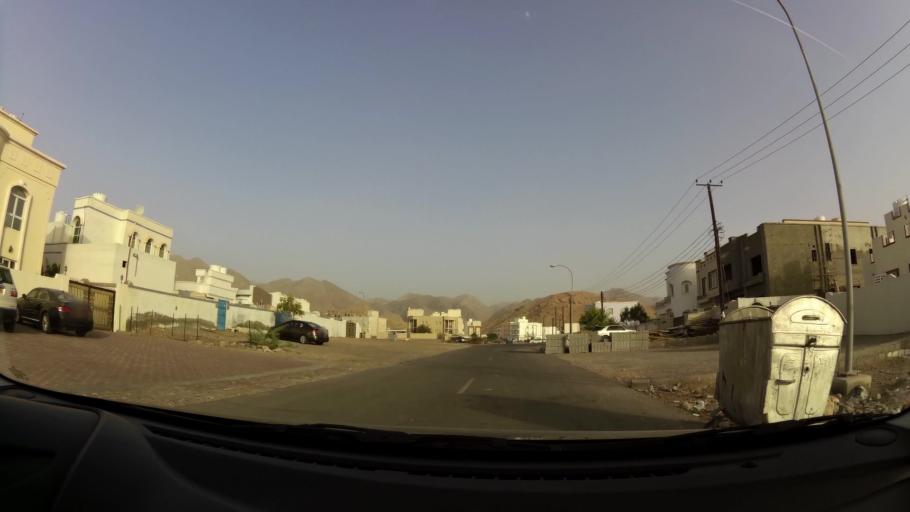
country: OM
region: Muhafazat Masqat
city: Bawshar
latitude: 23.5125
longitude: 58.3440
